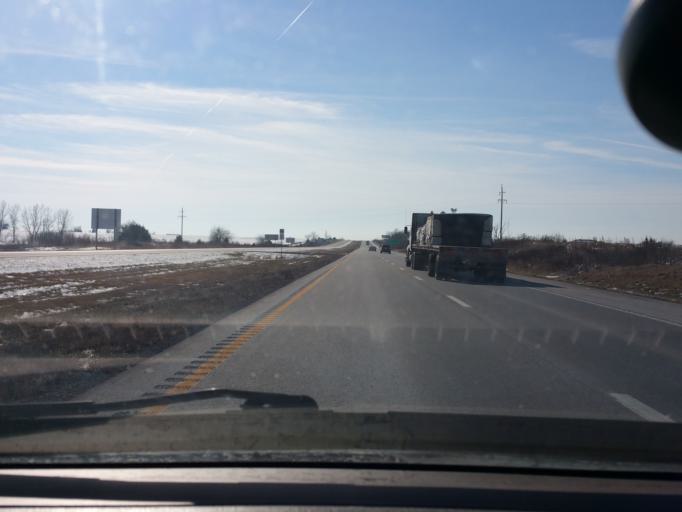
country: US
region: Missouri
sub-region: Clinton County
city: Cameron
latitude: 39.8449
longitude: -94.1808
